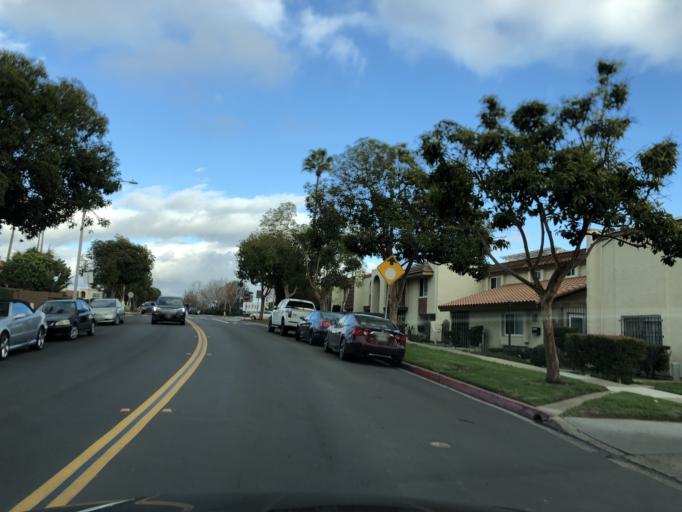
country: US
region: California
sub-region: San Diego County
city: La Jolla
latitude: 32.8162
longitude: -117.1837
